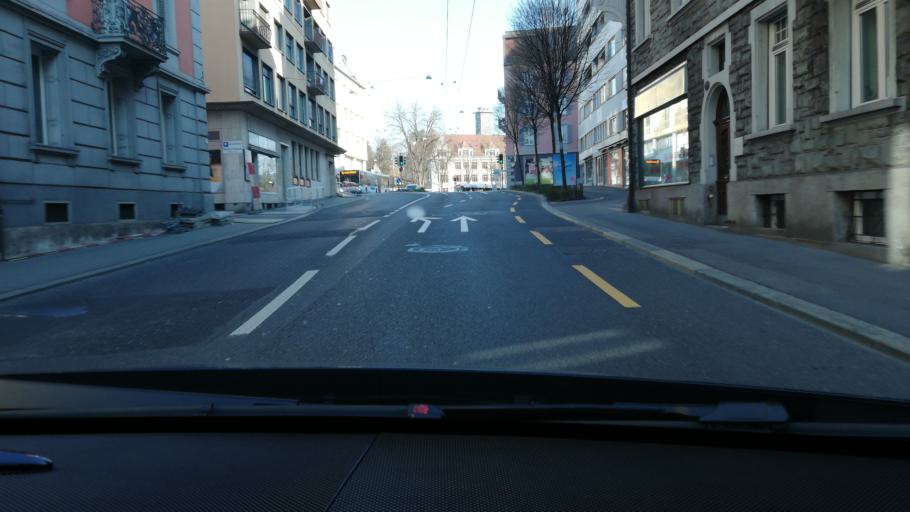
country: CH
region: Lucerne
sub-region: Lucerne-Stadt District
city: Luzern
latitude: 47.0604
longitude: 8.3090
